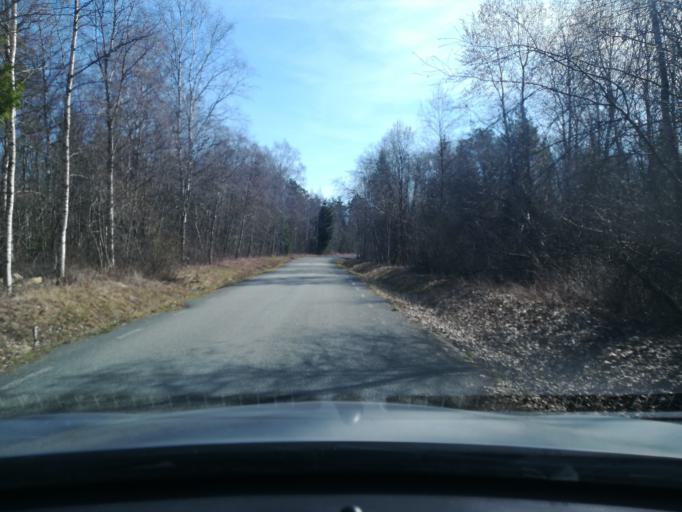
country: EE
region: Harju
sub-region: Saku vald
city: Saku
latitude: 59.2982
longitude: 24.6061
